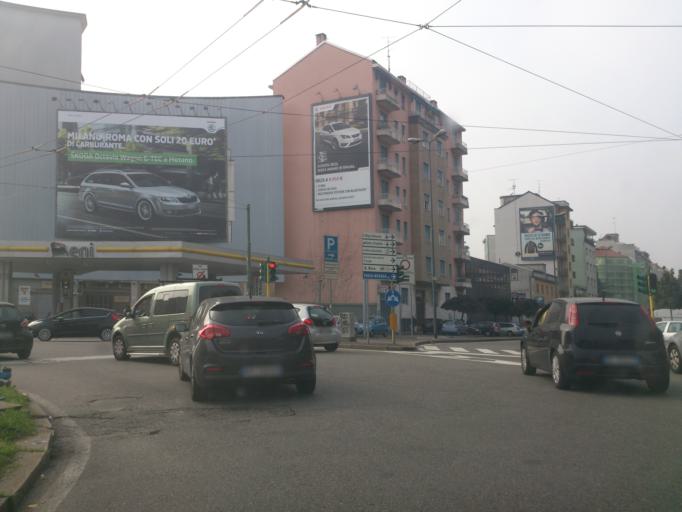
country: IT
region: Lombardy
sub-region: Citta metropolitana di Milano
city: Chiaravalle
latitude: 45.4444
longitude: 9.2239
